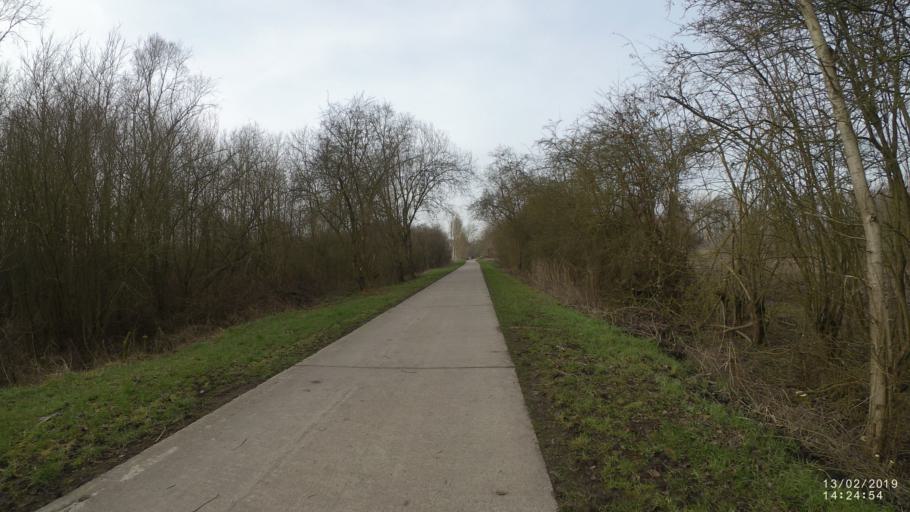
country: BE
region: Flanders
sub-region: Provincie Vlaams-Brabant
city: Zoutleeuw
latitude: 50.8423
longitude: 5.0687
